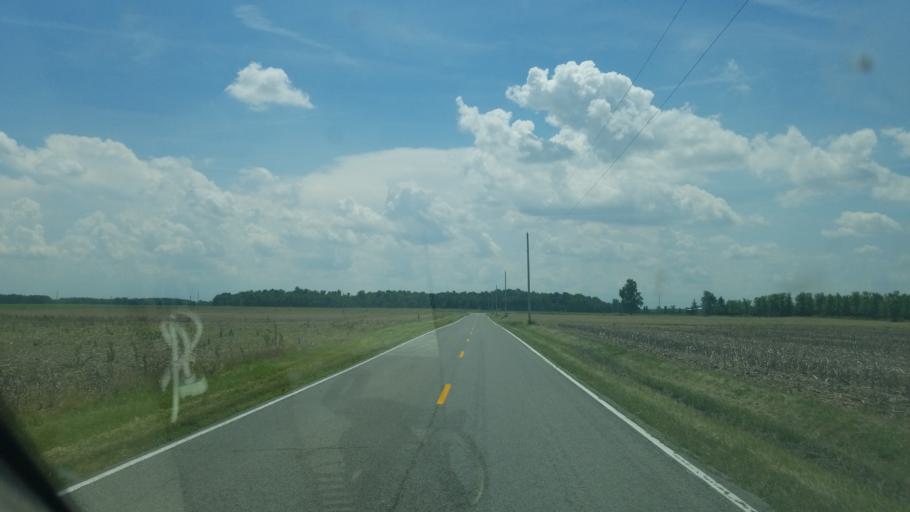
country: US
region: Ohio
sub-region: Hancock County
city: Arlington
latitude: 40.8948
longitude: -83.5948
